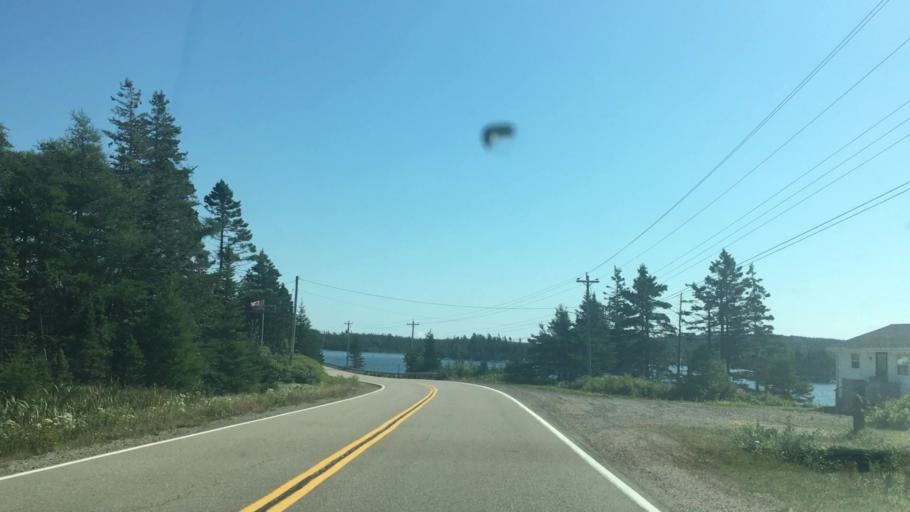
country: CA
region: Nova Scotia
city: Antigonish
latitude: 45.0233
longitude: -62.0205
